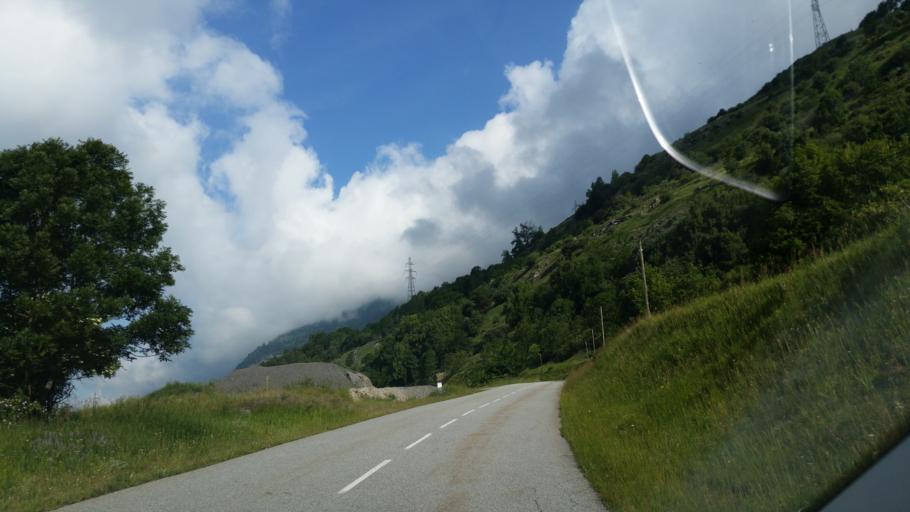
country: FR
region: Rhone-Alpes
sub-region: Departement de la Savoie
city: Modane
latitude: 45.2048
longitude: 6.6119
